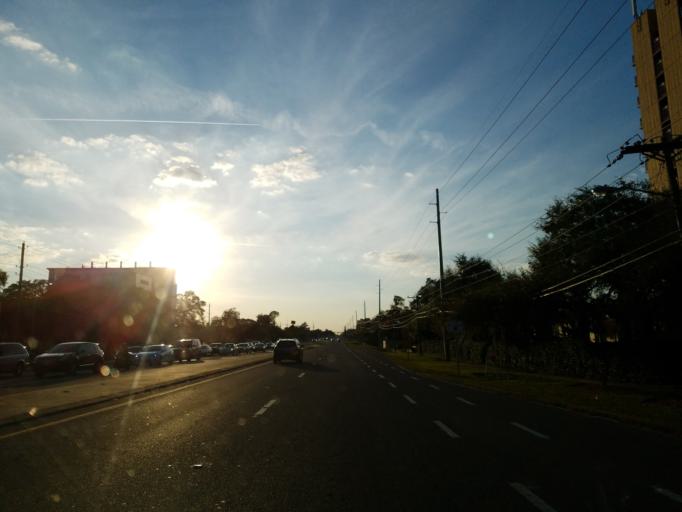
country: US
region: Florida
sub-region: Hillsborough County
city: University
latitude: 28.0692
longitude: -82.4153
